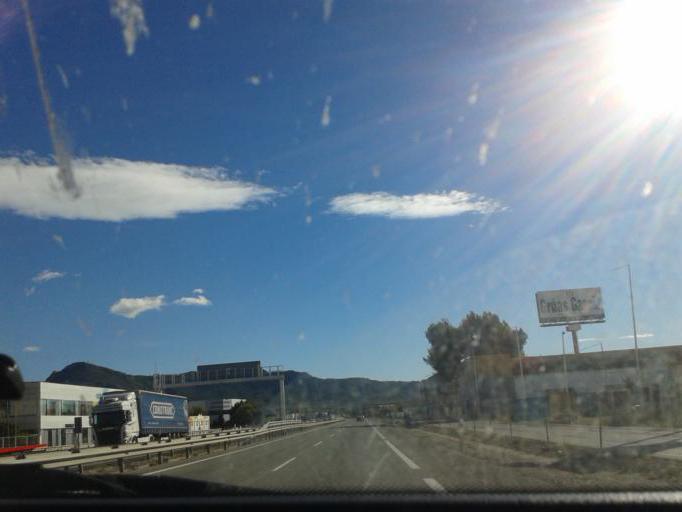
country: ES
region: Valencia
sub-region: Provincia de Alicante
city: Villena
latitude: 38.6219
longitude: -0.8510
